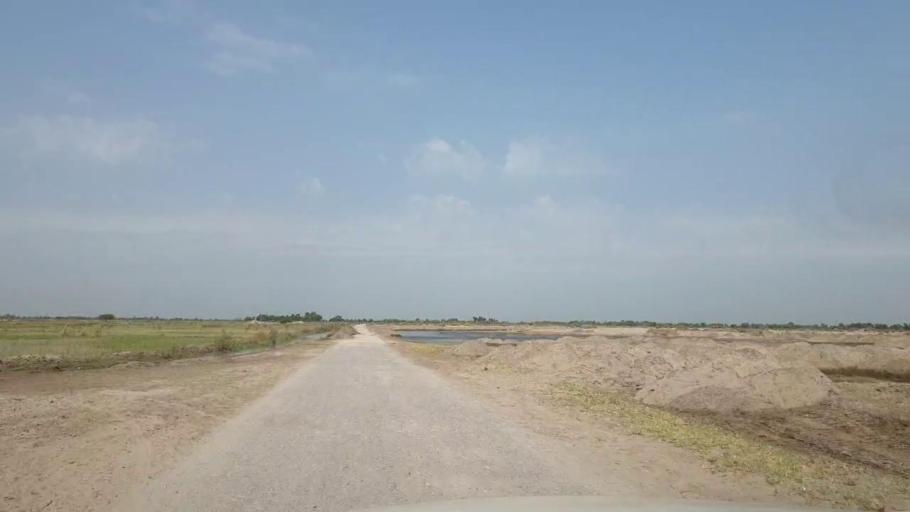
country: PK
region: Sindh
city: Ratodero
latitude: 27.8387
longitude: 68.2572
